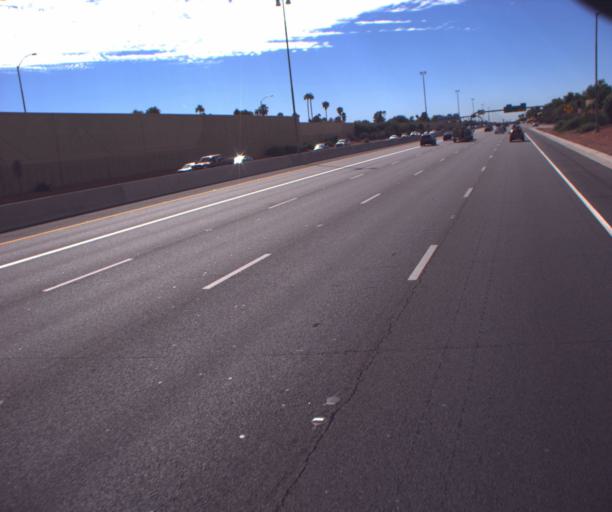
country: US
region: Arizona
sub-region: Maricopa County
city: Tempe
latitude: 33.3756
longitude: -111.8935
